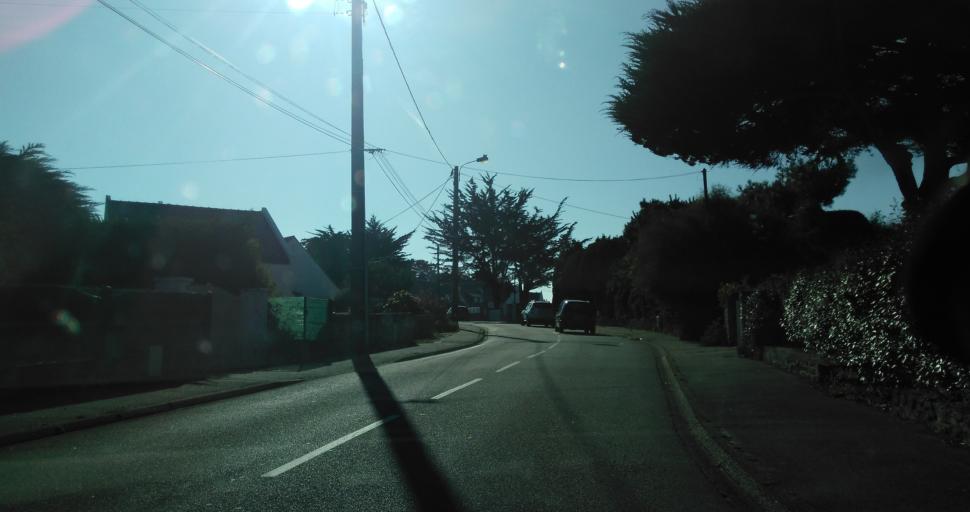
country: FR
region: Brittany
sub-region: Departement du Morbihan
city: Saint-Pierre-Quiberon
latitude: 47.5316
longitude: -3.1419
